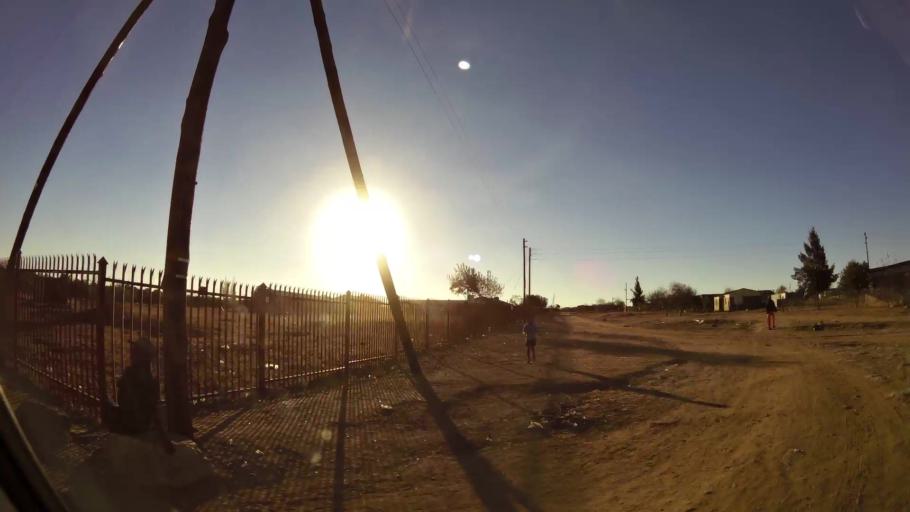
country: ZA
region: Limpopo
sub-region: Capricorn District Municipality
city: Polokwane
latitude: -23.8176
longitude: 29.3826
